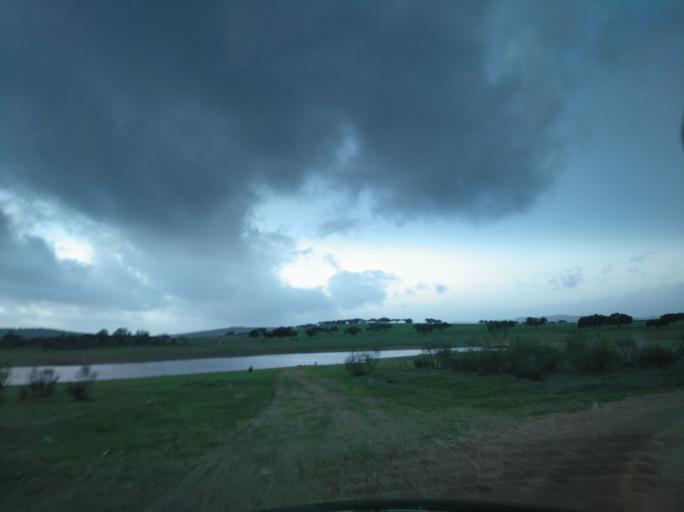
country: PT
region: Portalegre
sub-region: Campo Maior
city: Campo Maior
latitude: 39.1034
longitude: -7.1201
